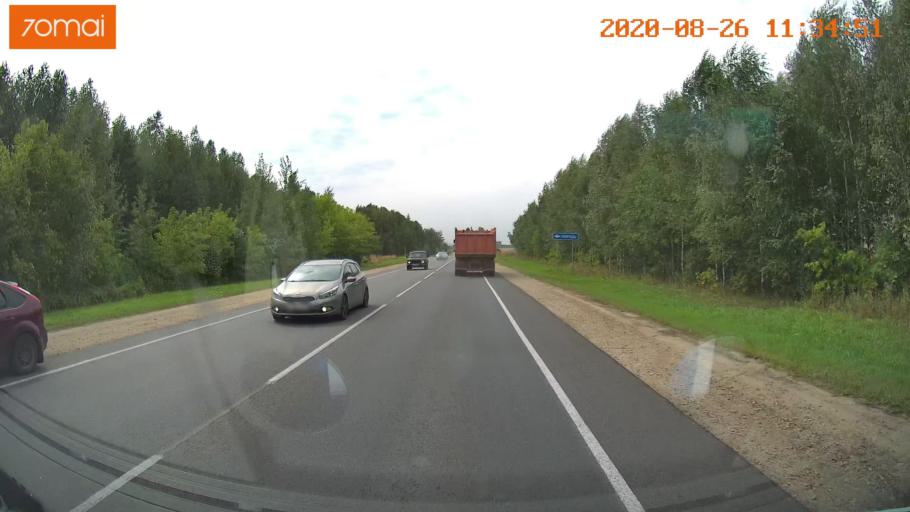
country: RU
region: Rjazan
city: Shilovo
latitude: 54.2804
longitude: 40.8391
